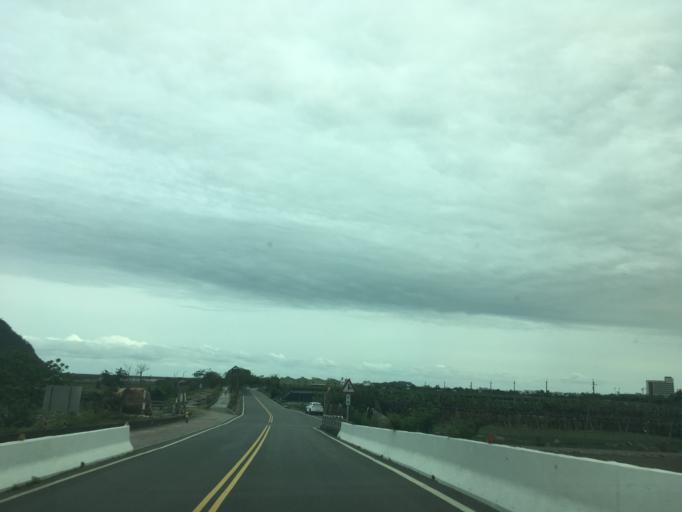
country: TW
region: Taiwan
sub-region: Taitung
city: Taitung
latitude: 22.8059
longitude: 121.1334
